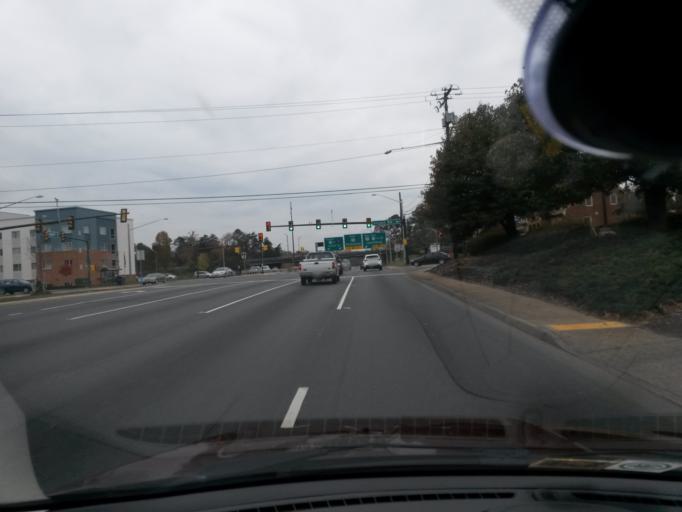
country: US
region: Virginia
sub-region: City of Charlottesville
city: Charlottesville
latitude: 38.0593
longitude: -78.4940
